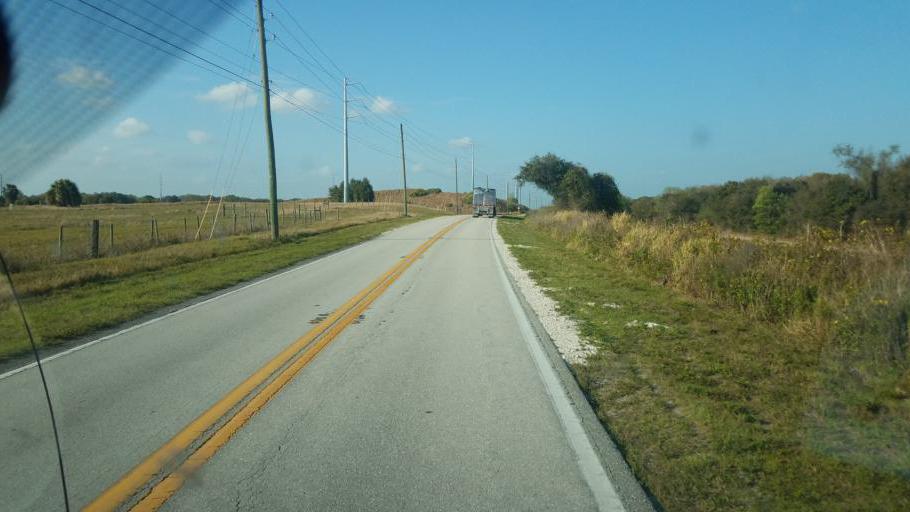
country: US
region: Florida
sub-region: Polk County
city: Mulberry
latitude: 27.7345
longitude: -81.9734
